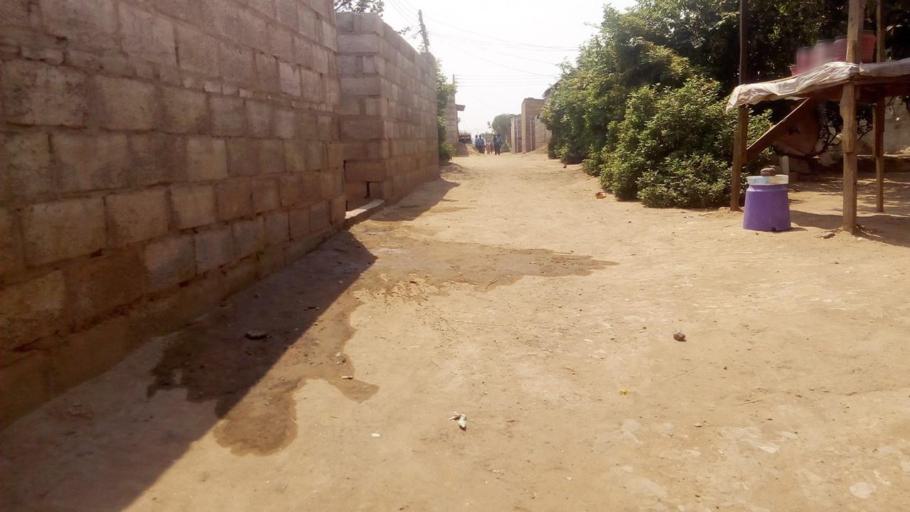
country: ZM
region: Lusaka
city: Lusaka
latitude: -15.3582
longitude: 28.2925
